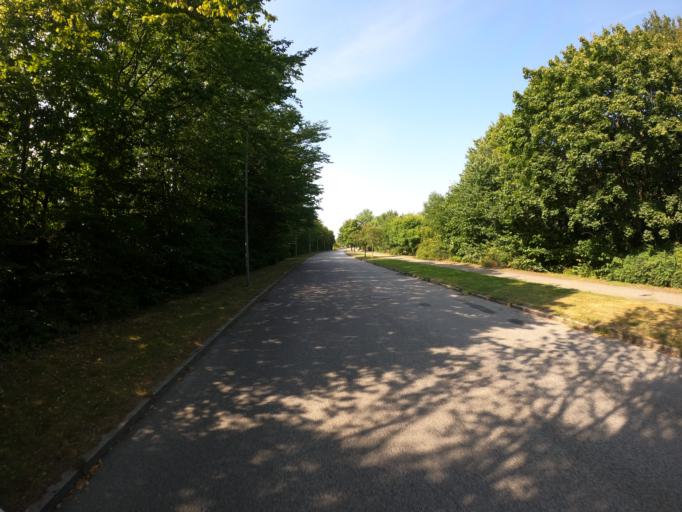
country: SE
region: Skane
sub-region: Lunds Kommun
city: Lund
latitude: 55.7241
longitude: 13.1706
